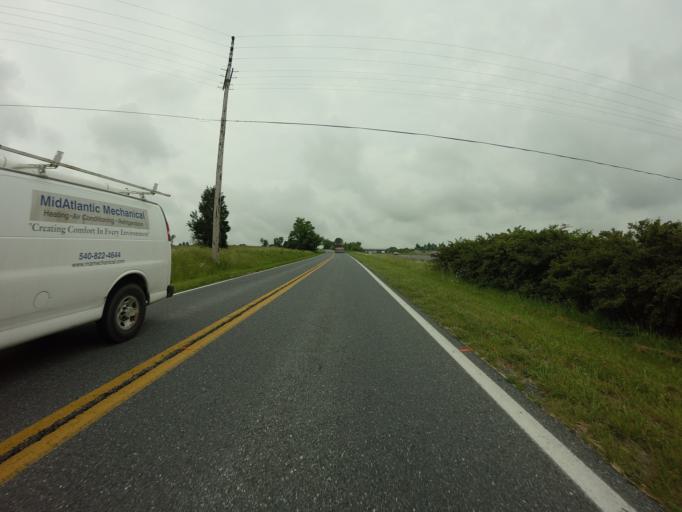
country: US
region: Maryland
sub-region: Frederick County
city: Ballenger Creek
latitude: 39.3789
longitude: -77.4713
